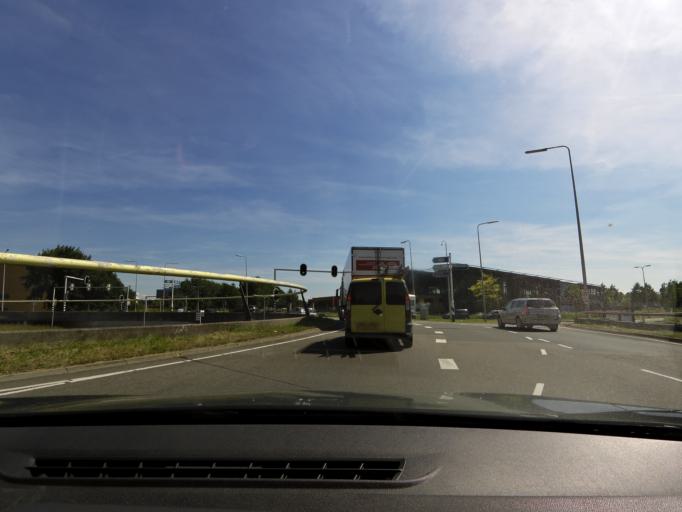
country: NL
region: South Holland
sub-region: Gemeente Spijkenisse
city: Spijkenisse
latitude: 51.8510
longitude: 4.3102
